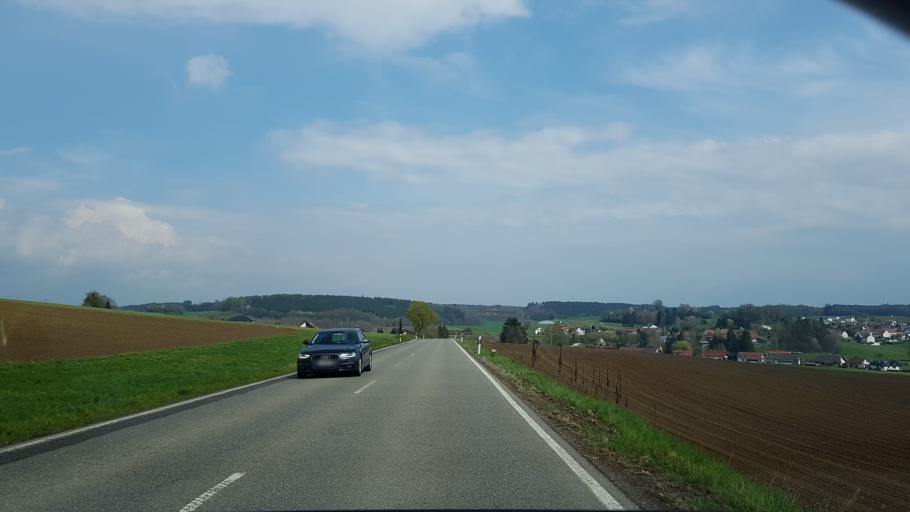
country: DE
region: Baden-Wuerttemberg
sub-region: Tuebingen Region
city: Wain
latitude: 48.2133
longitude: 10.0068
